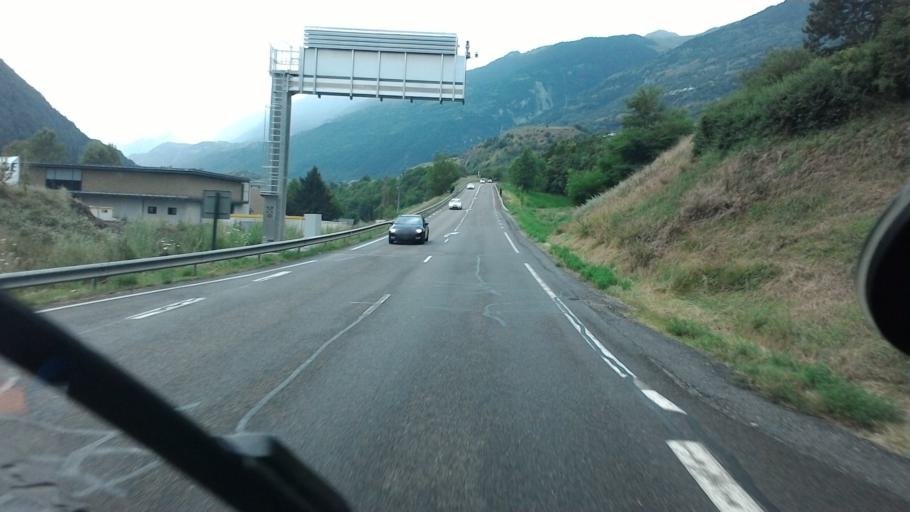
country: FR
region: Rhone-Alpes
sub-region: Departement de la Savoie
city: Aime
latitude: 45.5533
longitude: 6.6449
